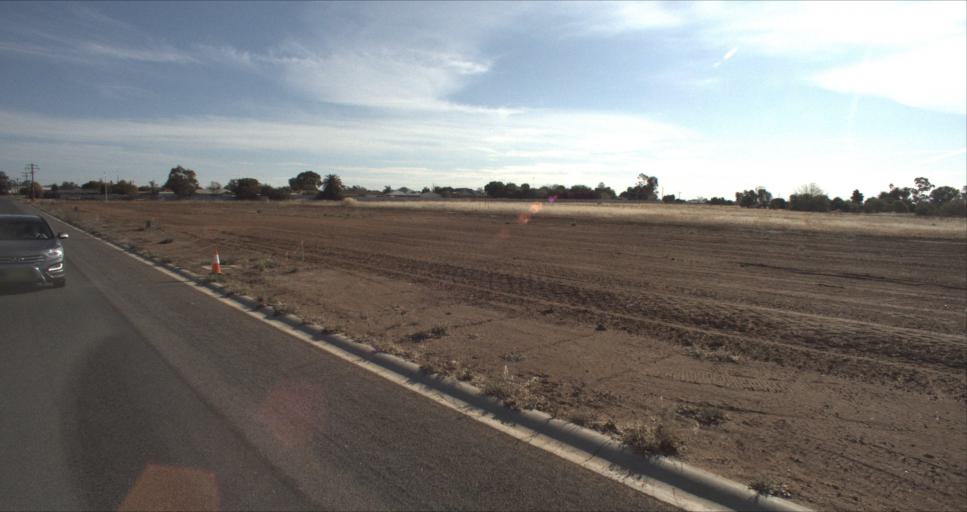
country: AU
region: New South Wales
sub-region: Leeton
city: Leeton
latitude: -34.5427
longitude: 146.3998
